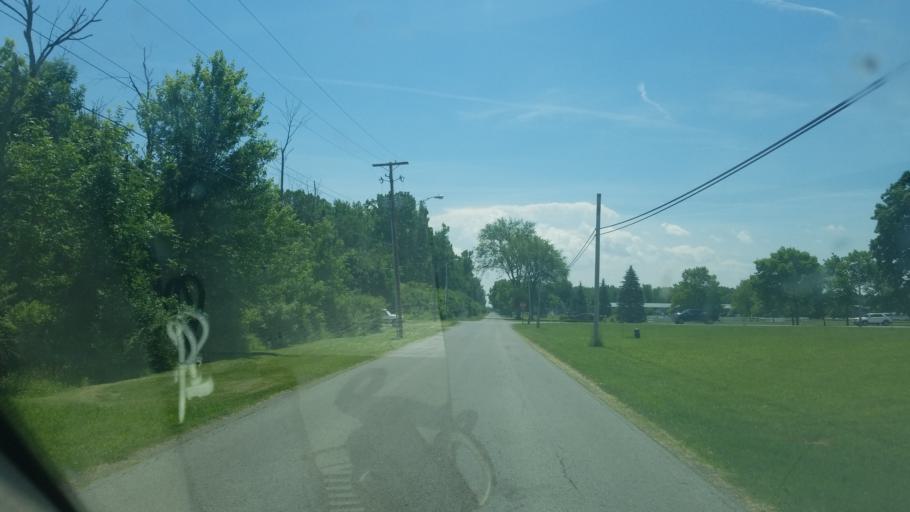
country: US
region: Ohio
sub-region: Hancock County
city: Findlay
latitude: 41.0088
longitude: -83.6362
